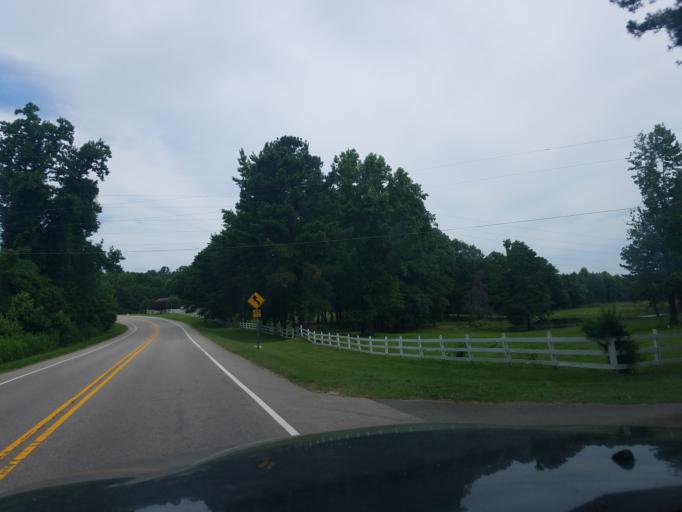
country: US
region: North Carolina
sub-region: Durham County
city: Durham
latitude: 36.1196
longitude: -78.9317
